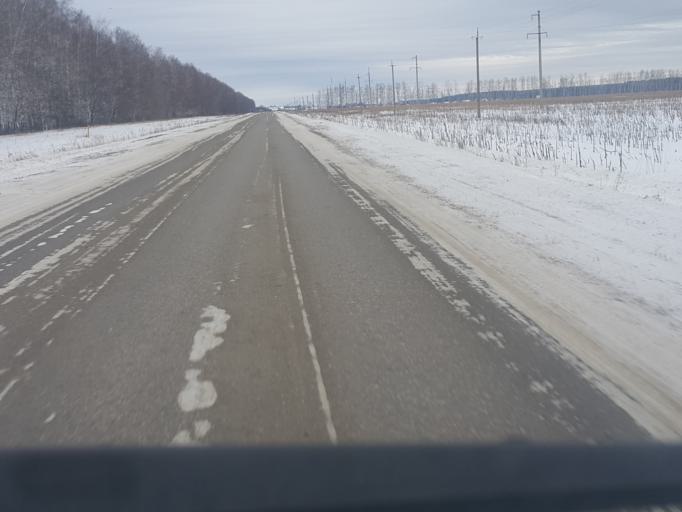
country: RU
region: Tambov
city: Rasskazovo
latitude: 52.8191
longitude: 41.7978
